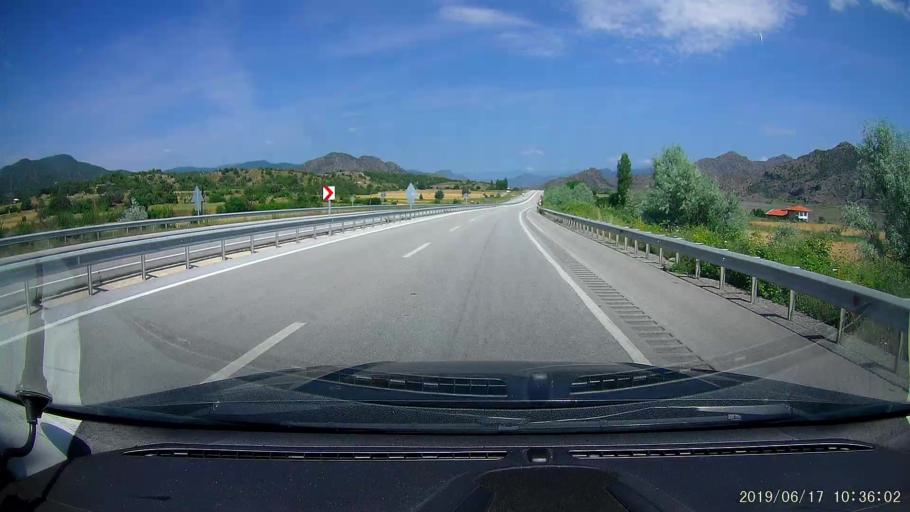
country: TR
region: Corum
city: Osmancik
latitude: 40.9733
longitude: 34.6892
